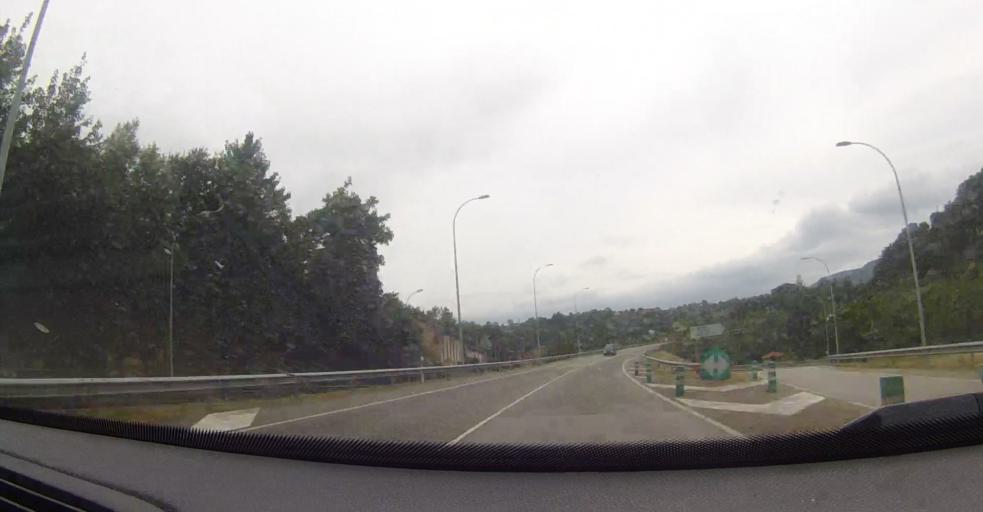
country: ES
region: Asturias
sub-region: Province of Asturias
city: Pilona
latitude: 43.3460
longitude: -5.3529
